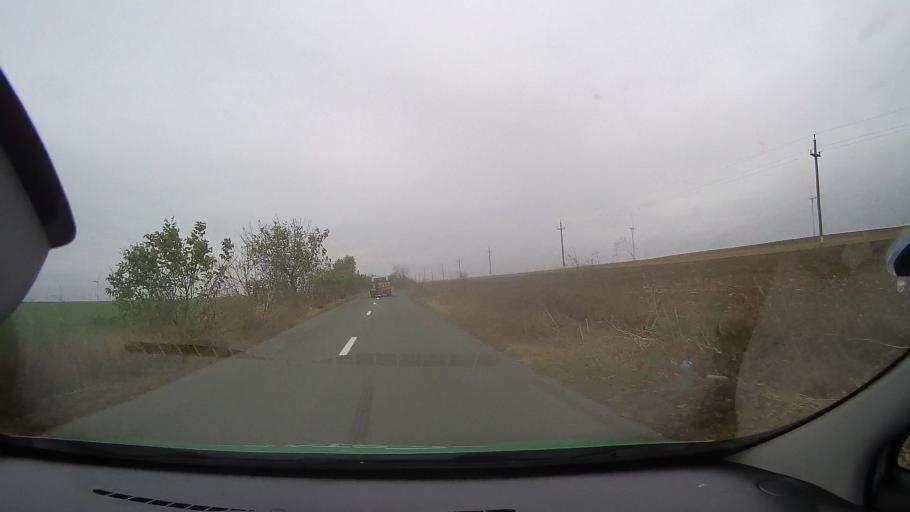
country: RO
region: Constanta
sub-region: Comuna Targusor
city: Targusor
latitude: 44.4749
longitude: 28.3817
